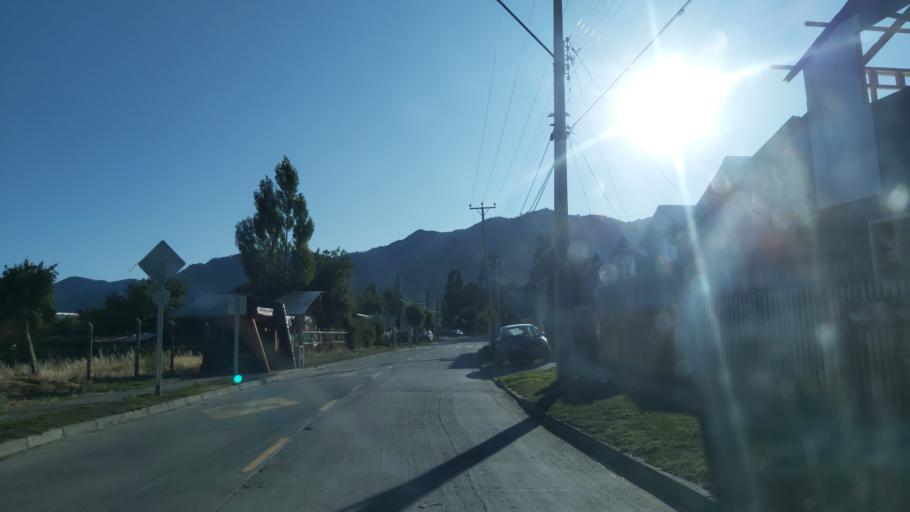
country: AR
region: Neuquen
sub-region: Departamento de Loncopue
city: Loncopue
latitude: -38.4491
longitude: -71.3684
